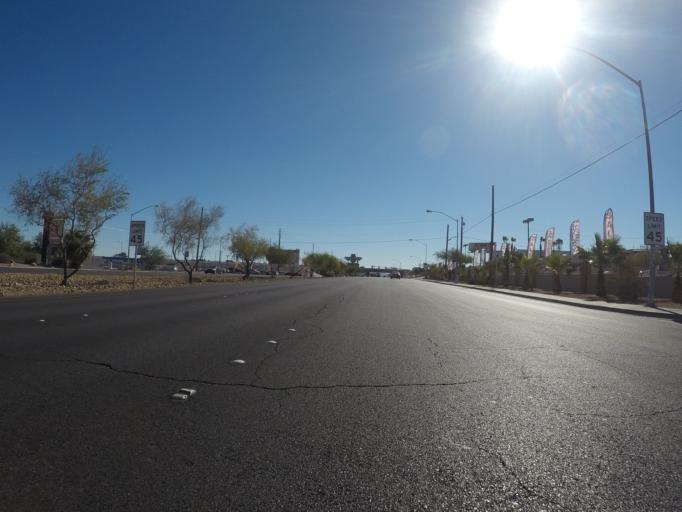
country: US
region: Nevada
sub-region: Clark County
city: Winchester
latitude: 36.1381
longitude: -115.0931
